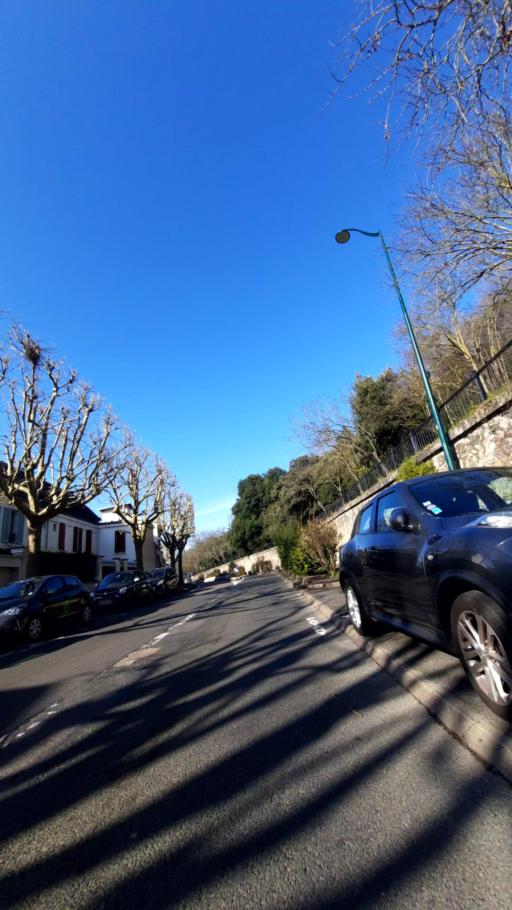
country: FR
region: Ile-de-France
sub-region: Departement du Val-de-Marne
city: Maisons-Alfort
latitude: 48.8182
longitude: 2.4405
